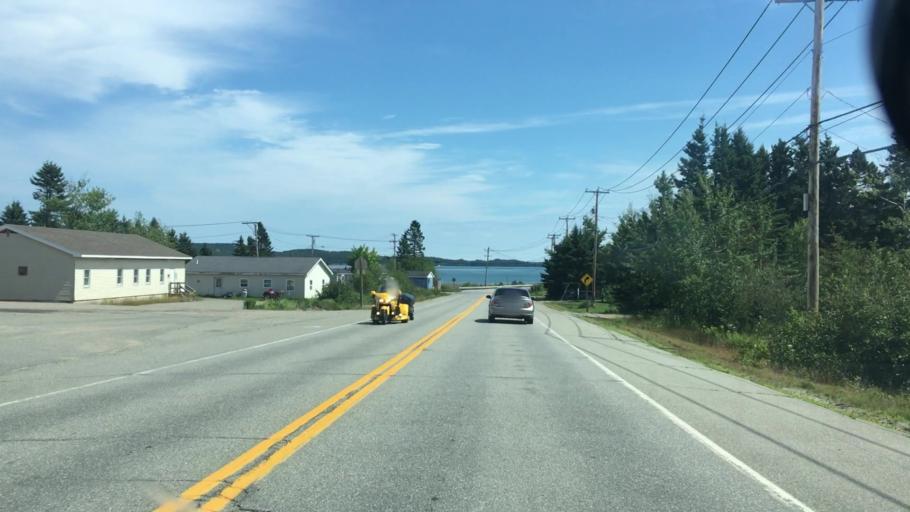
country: US
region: Maine
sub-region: Washington County
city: Eastport
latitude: 44.9556
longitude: -67.0434
